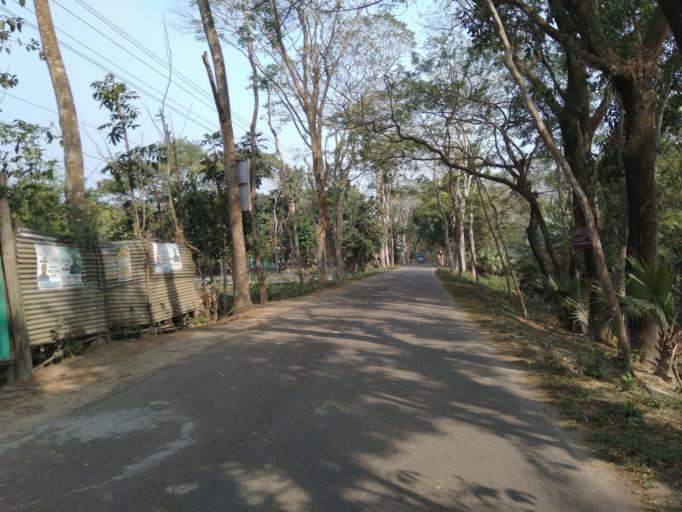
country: BD
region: Barisal
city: Mehendiganj
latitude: 22.9614
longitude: 90.4146
